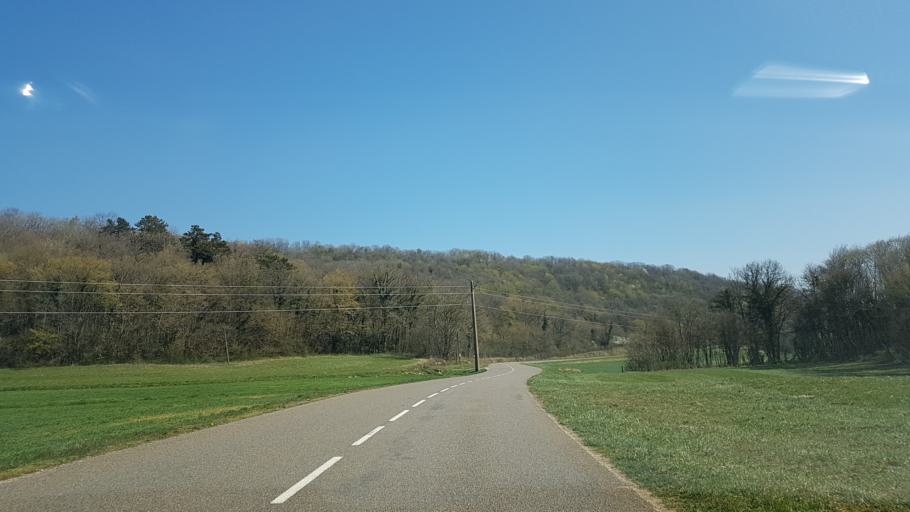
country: FR
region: Bourgogne
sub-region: Departement de Saone-et-Loire
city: Cuiseaux
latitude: 46.4582
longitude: 5.4093
